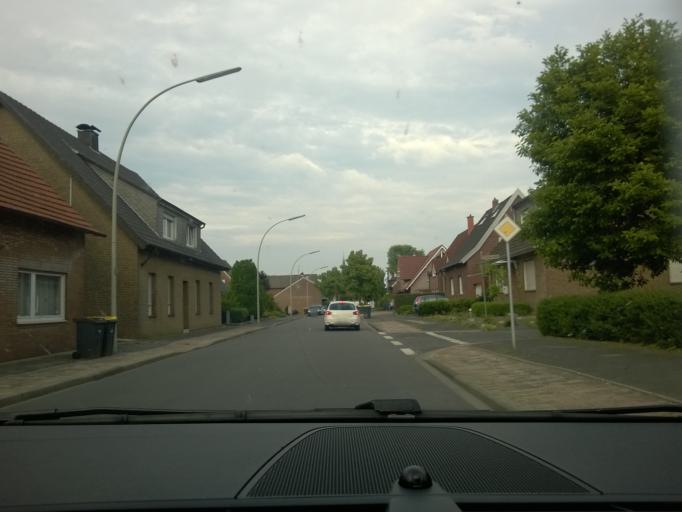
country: DE
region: North Rhine-Westphalia
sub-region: Regierungsbezirk Munster
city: Gescher
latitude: 51.9547
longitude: 6.9945
